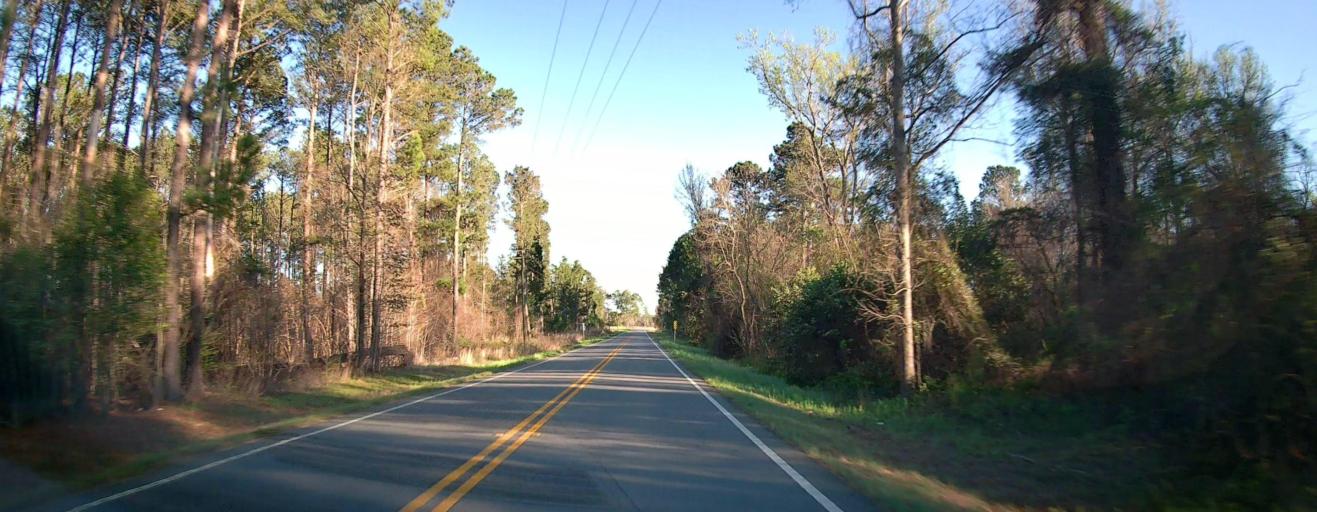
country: US
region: Georgia
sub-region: Pulaski County
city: Hawkinsville
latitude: 32.2102
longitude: -83.3801
